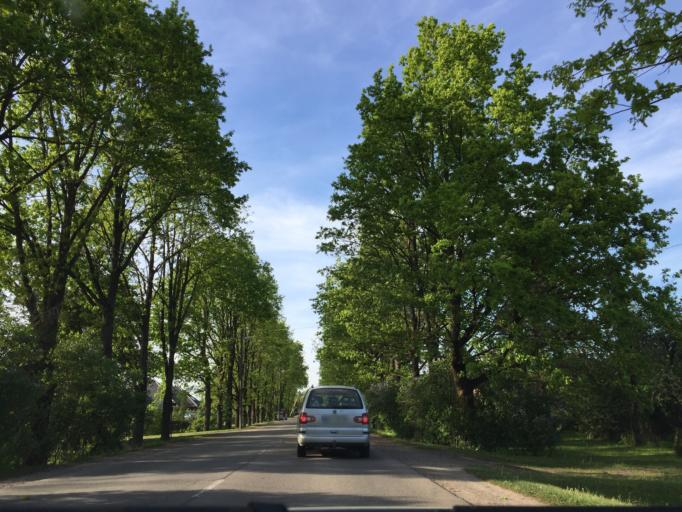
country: LV
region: Jelgava
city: Jelgava
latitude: 56.6261
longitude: 23.6921
